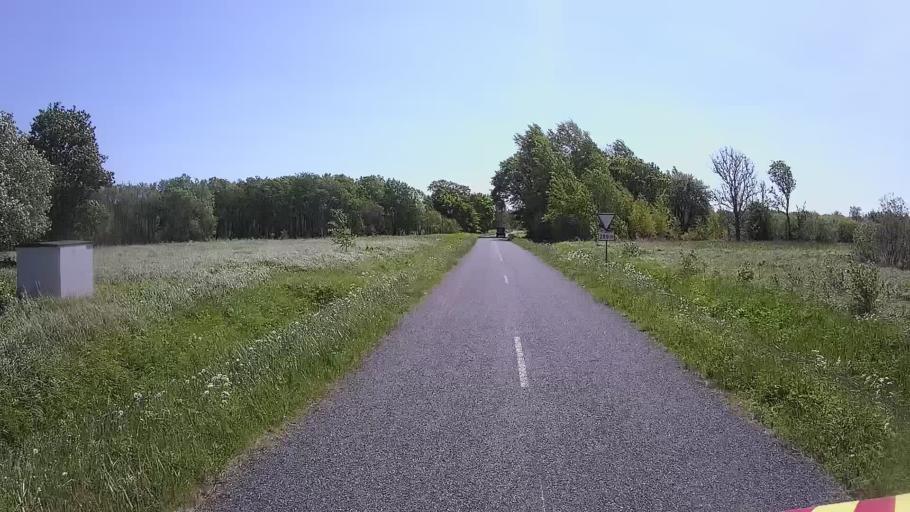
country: LV
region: Dundaga
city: Dundaga
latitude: 57.9367
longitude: 22.0926
